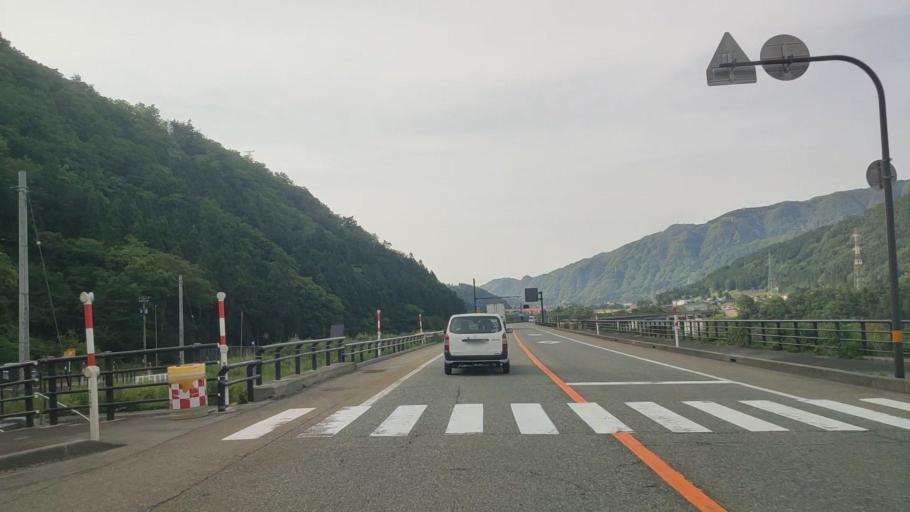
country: JP
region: Toyama
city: Yatsuomachi-higashikumisaka
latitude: 36.5109
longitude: 137.2283
